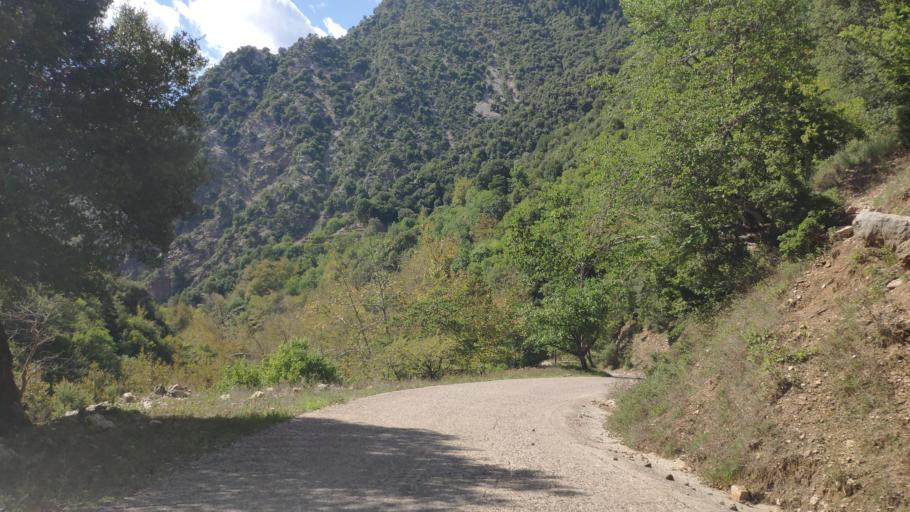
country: GR
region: Central Greece
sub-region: Nomos Evrytanias
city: Kerasochori
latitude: 39.1373
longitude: 21.6442
